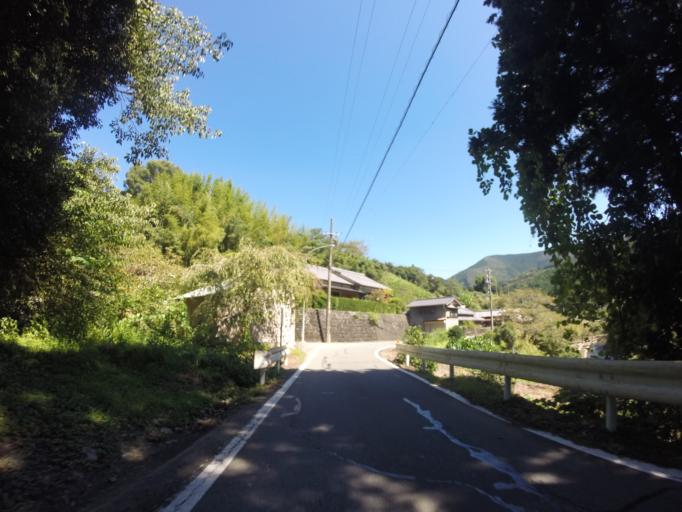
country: JP
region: Shizuoka
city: Kanaya
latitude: 34.9264
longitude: 138.1378
